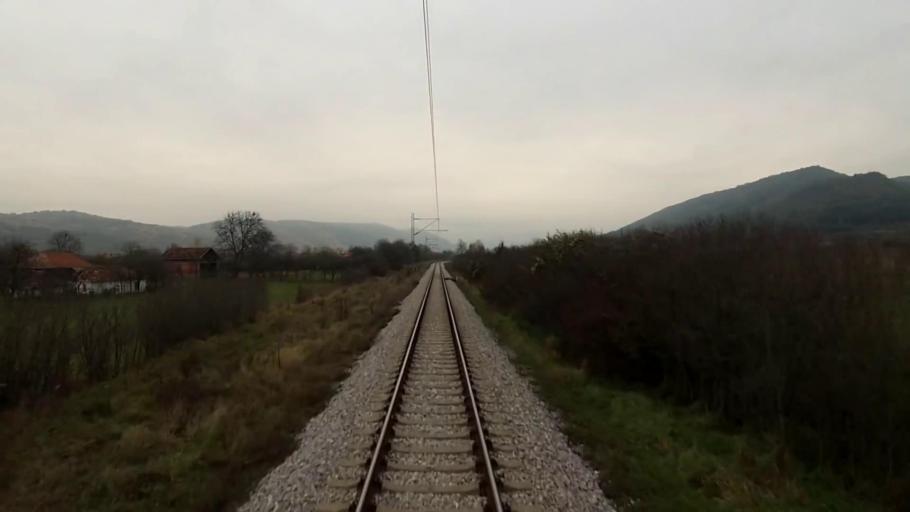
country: RS
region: Central Serbia
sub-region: Pirotski Okrug
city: Dimitrovgrad
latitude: 43.0039
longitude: 22.8149
